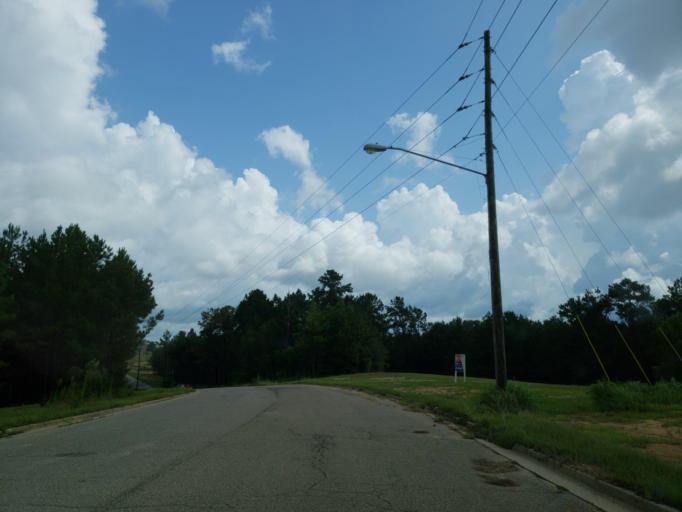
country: US
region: Mississippi
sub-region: Lamar County
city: West Hattiesburg
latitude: 31.3119
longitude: -89.3941
